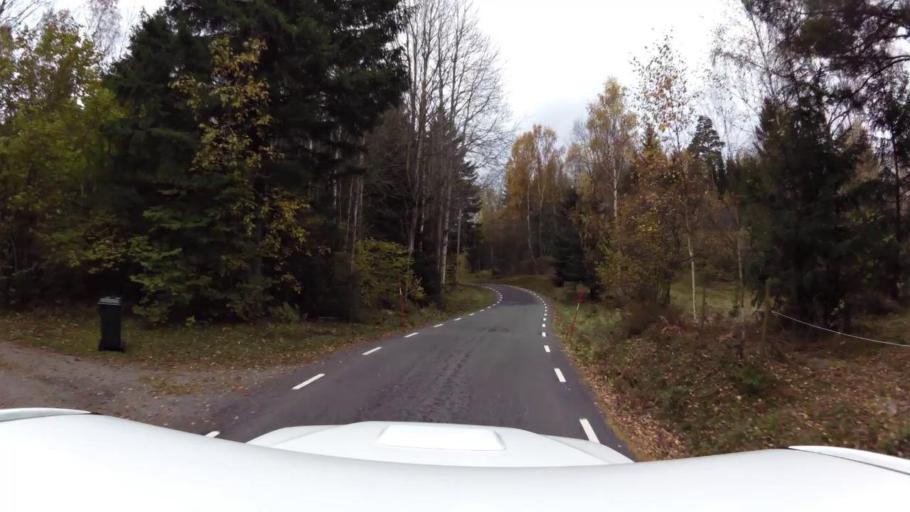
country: SE
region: OEstergoetland
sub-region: Linkopings Kommun
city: Ljungsbro
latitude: 58.5737
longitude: 15.4620
